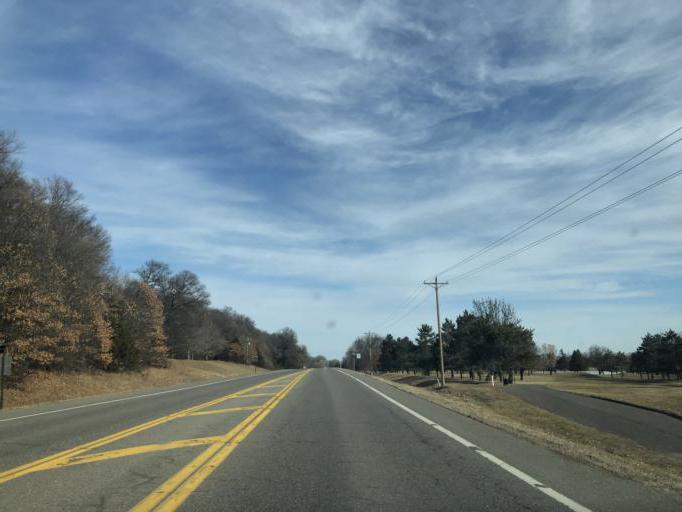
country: US
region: Minnesota
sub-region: Sherburne County
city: Becker
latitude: 45.4091
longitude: -93.8707
